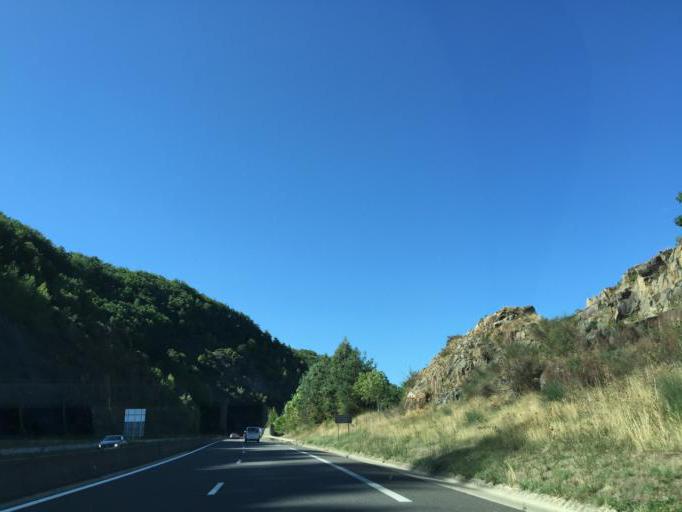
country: FR
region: Languedoc-Roussillon
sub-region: Departement de la Lozere
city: La Canourgue
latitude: 44.4513
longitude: 3.1929
